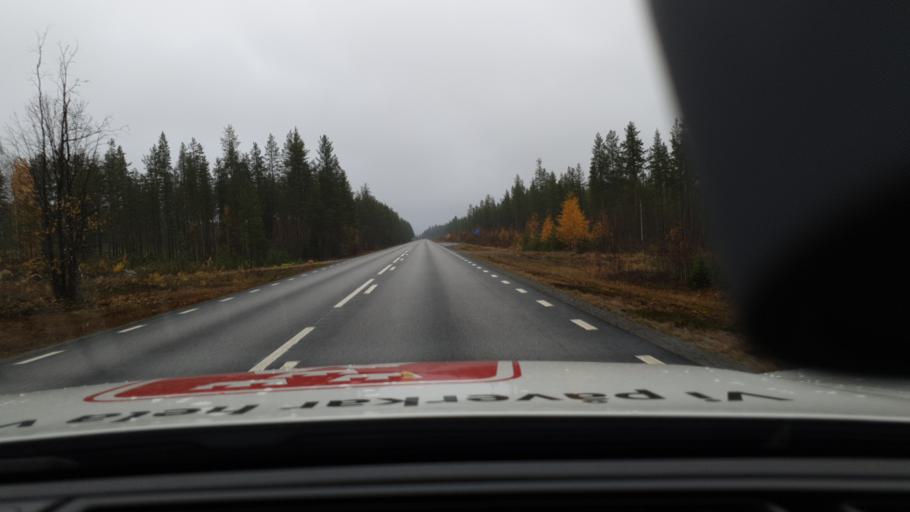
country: SE
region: Norrbotten
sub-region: Overkalix Kommun
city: OEverkalix
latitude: 66.6128
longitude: 22.2398
